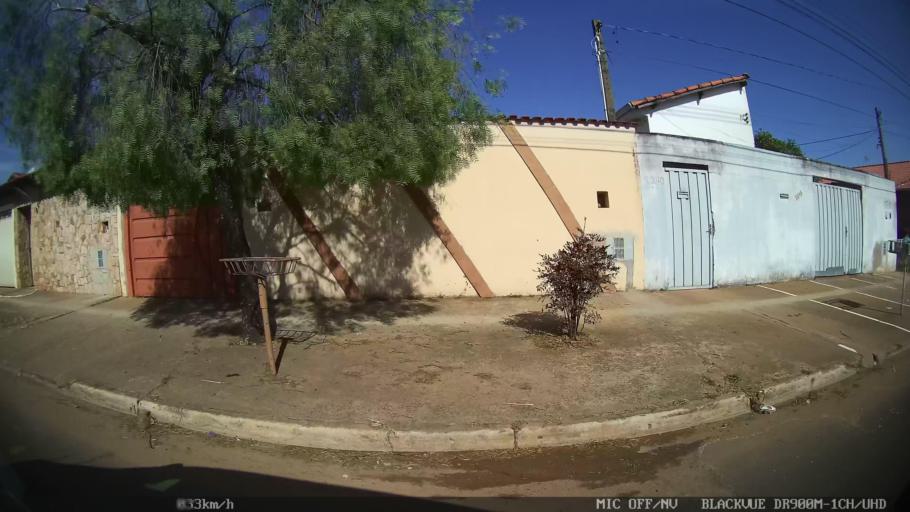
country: BR
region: Sao Paulo
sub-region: Franca
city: Franca
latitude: -20.5078
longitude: -47.4225
